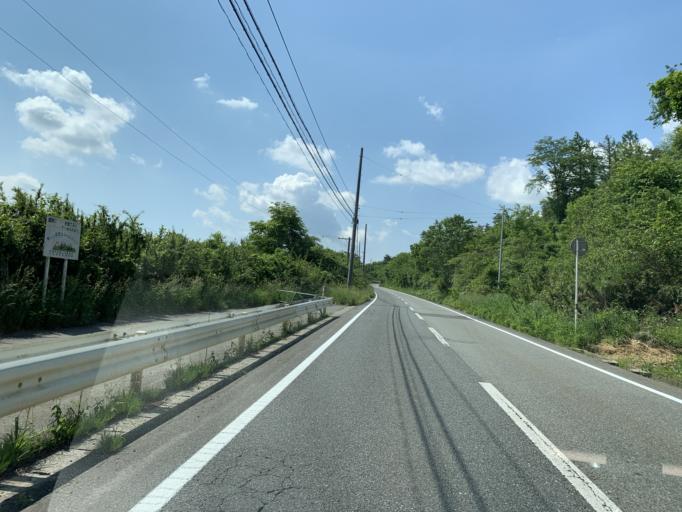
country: JP
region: Miyagi
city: Furukawa
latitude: 38.7208
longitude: 140.9485
